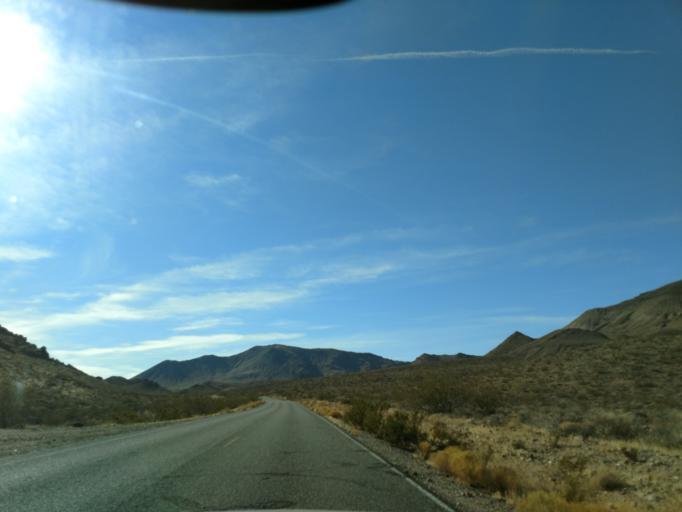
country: US
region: Nevada
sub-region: Nye County
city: Beatty
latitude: 36.8092
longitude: -116.9109
